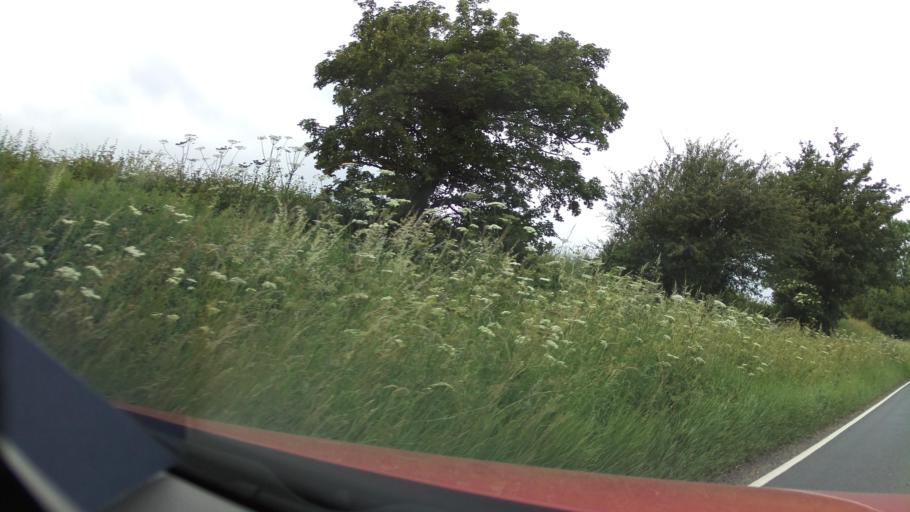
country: GB
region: England
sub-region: Leicestershire
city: Grimston
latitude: 52.7743
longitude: -0.9921
